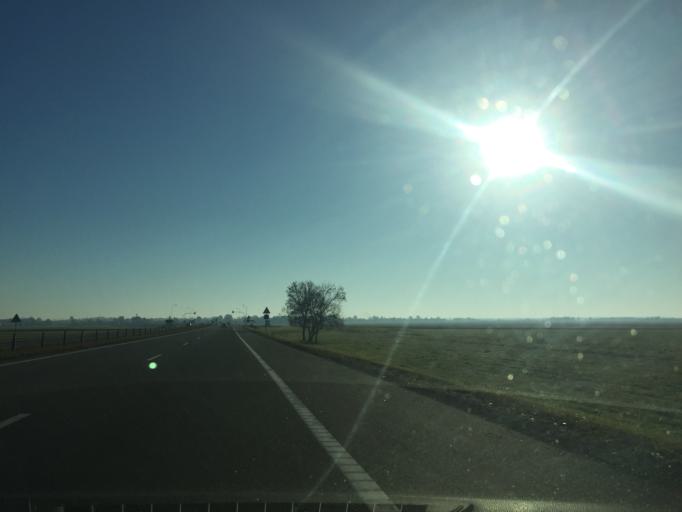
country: BY
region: Minsk
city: Smilavichy
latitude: 53.7596
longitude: 27.9531
